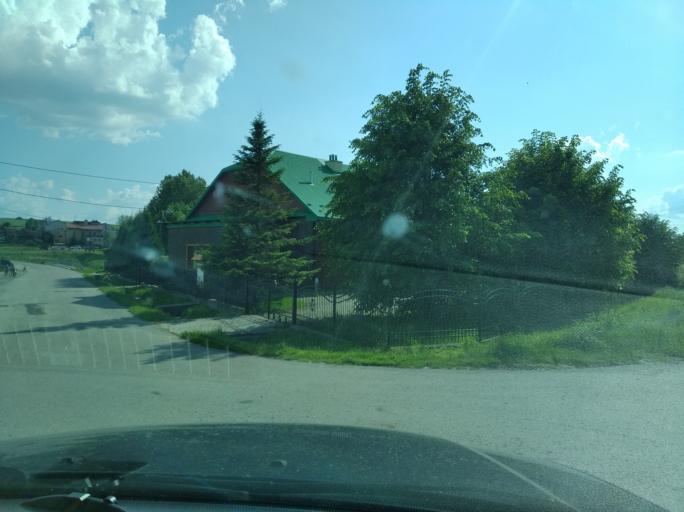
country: PL
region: Subcarpathian Voivodeship
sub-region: Powiat jaroslawski
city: Rokietnica
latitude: 49.9255
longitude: 22.6942
